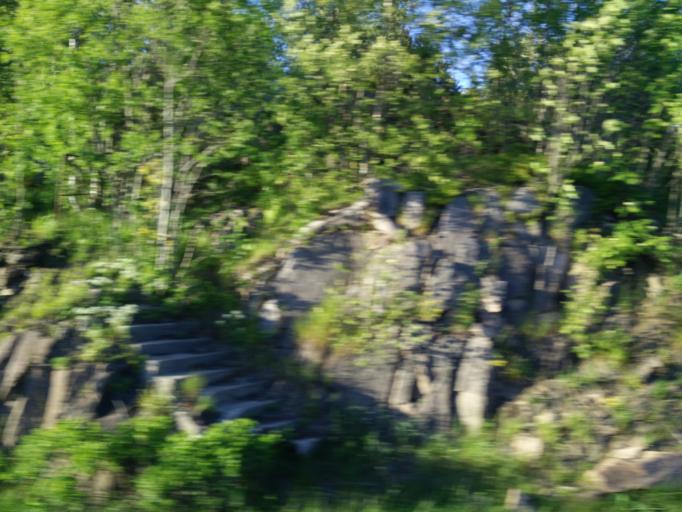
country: NO
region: Akershus
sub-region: Baerum
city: Skui
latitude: 59.9643
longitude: 10.3434
